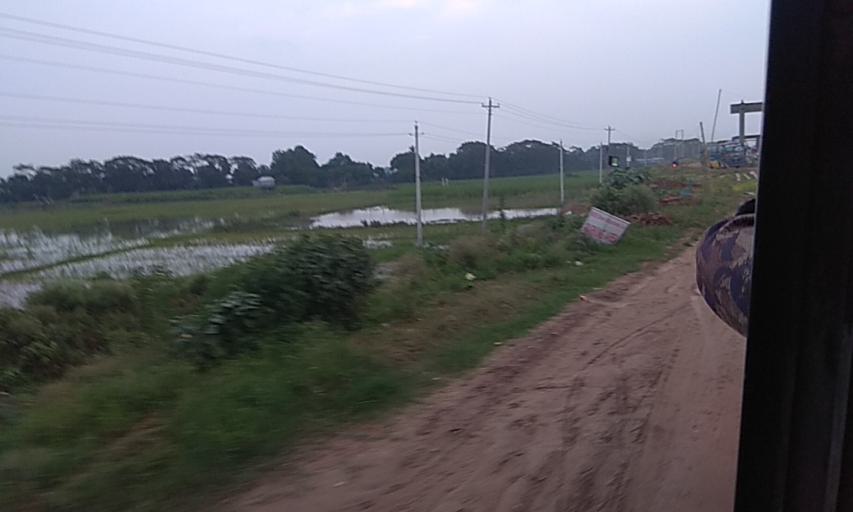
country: BD
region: Dhaka
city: Char Bhadrasan
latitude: 23.3823
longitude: 90.0019
